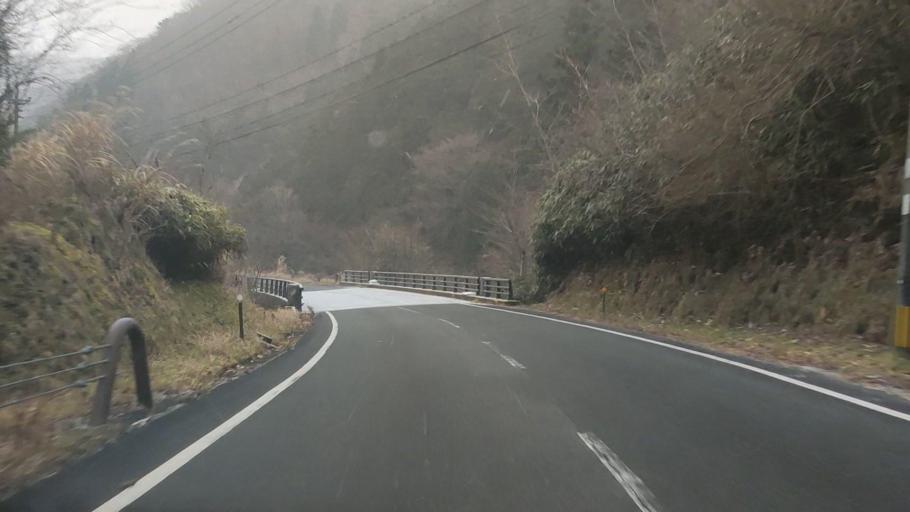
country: JP
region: Kumamoto
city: Matsubase
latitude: 32.5641
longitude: 130.9134
